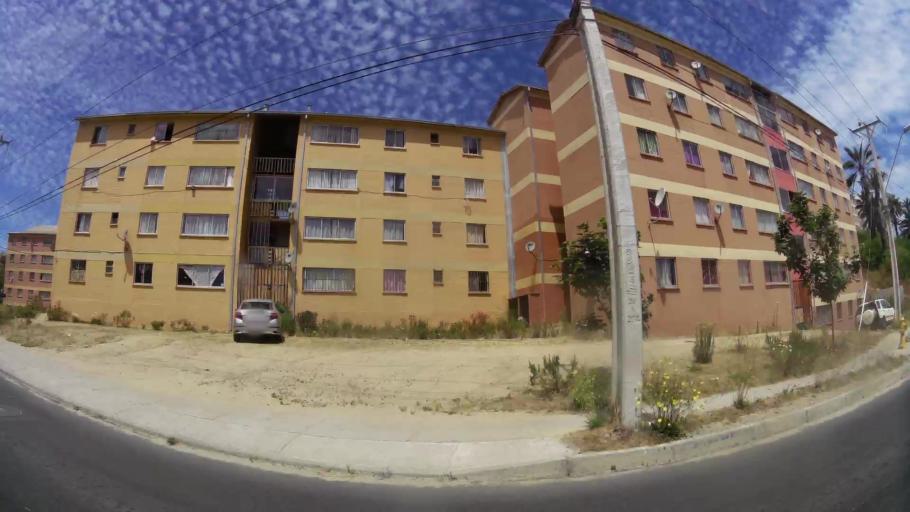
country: CL
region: Valparaiso
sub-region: Provincia de Valparaiso
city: Vina del Mar
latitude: -33.0610
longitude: -71.5620
